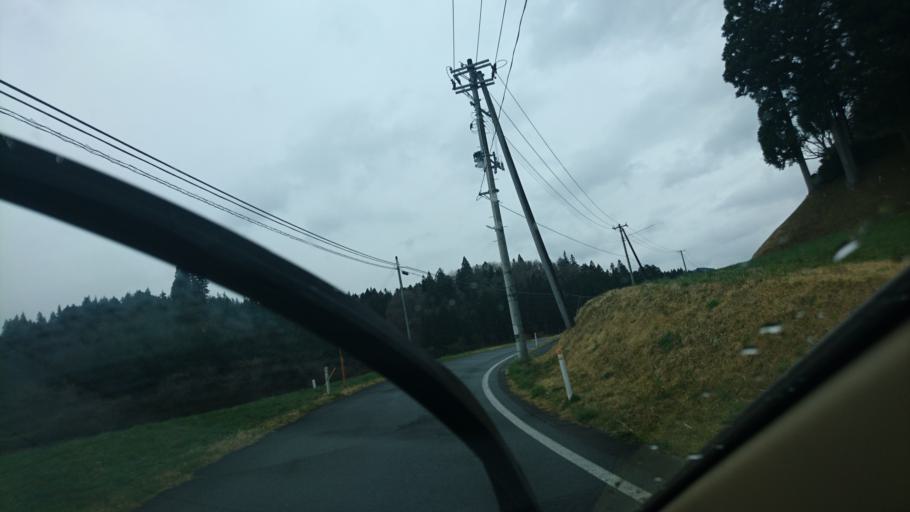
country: JP
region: Iwate
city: Ichinoseki
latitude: 38.9425
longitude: 141.3321
